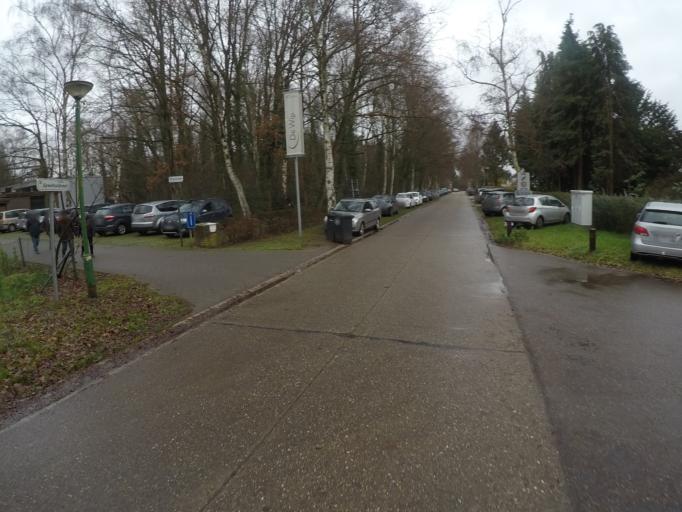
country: BE
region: Flanders
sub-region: Provincie Antwerpen
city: Schilde
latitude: 51.2296
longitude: 4.5772
